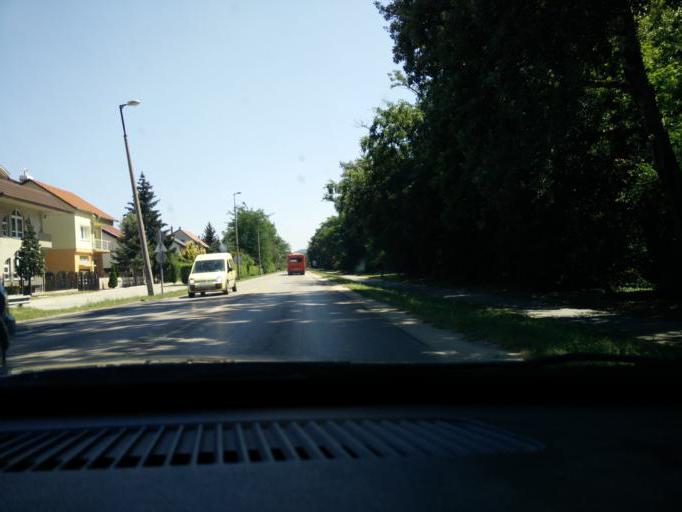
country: HU
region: Komarom-Esztergom
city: Tata
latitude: 47.6432
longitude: 18.3396
